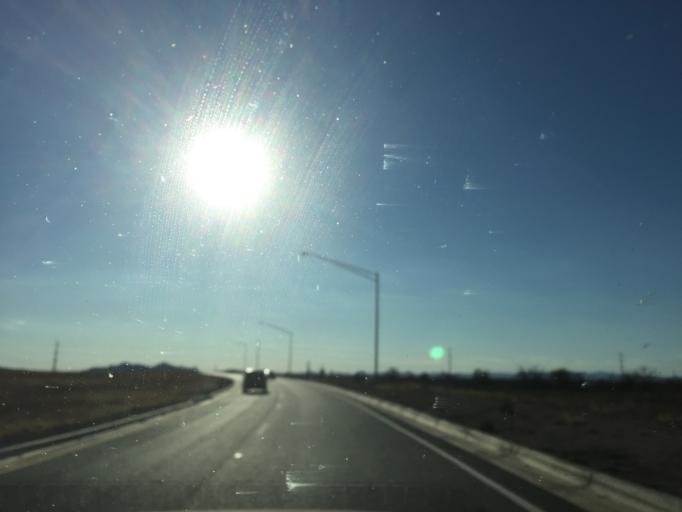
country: US
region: Arizona
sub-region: Maricopa County
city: Anthem
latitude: 33.7697
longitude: -112.1336
